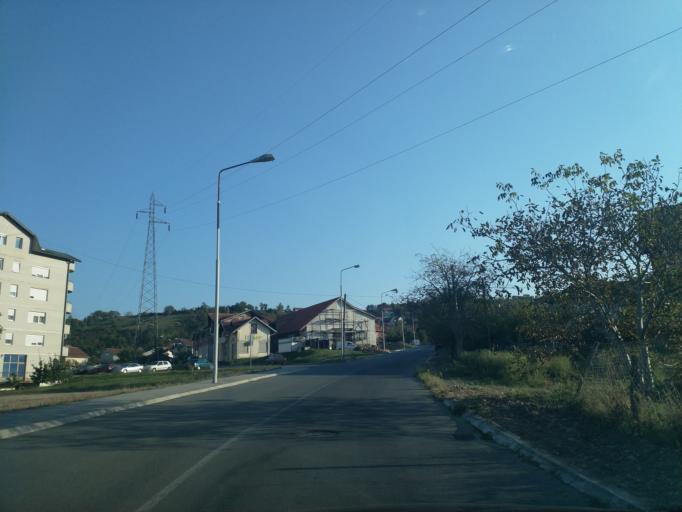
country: RS
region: Central Serbia
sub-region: Rasinski Okrug
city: Trstenik
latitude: 43.6094
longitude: 21.0076
